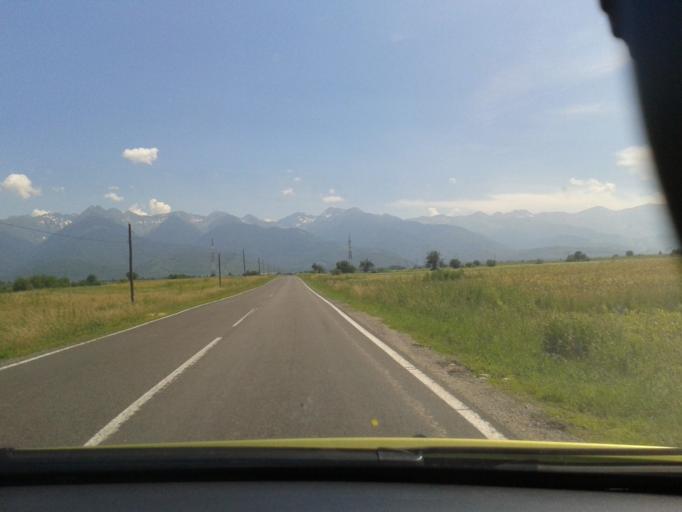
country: RO
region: Sibiu
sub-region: Comuna Carta
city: Carta
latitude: 45.7512
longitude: 24.5759
